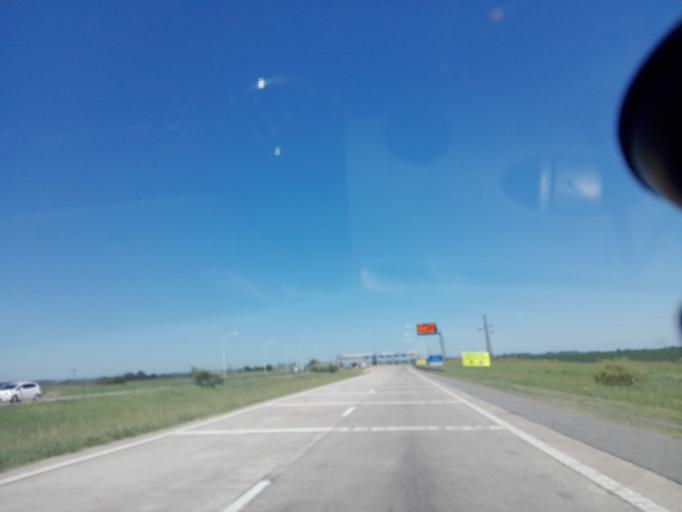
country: AR
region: Santa Fe
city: Carcarana
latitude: -32.8770
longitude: -61.1656
